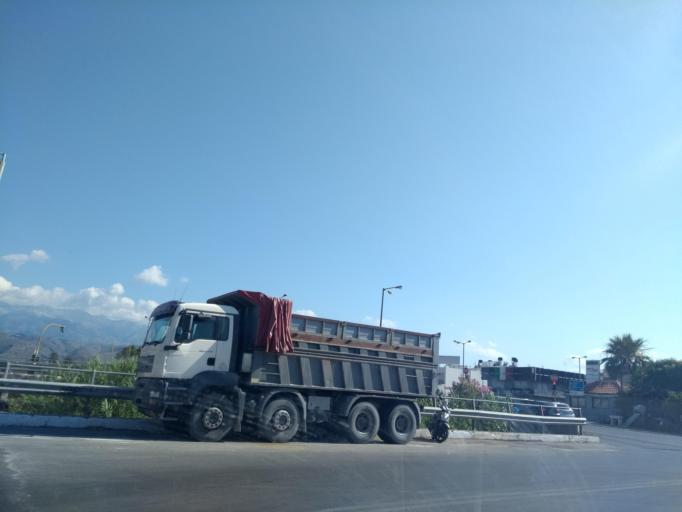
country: GR
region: Crete
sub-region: Nomos Chanias
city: Perivolia
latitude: 35.5073
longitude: 24.0040
